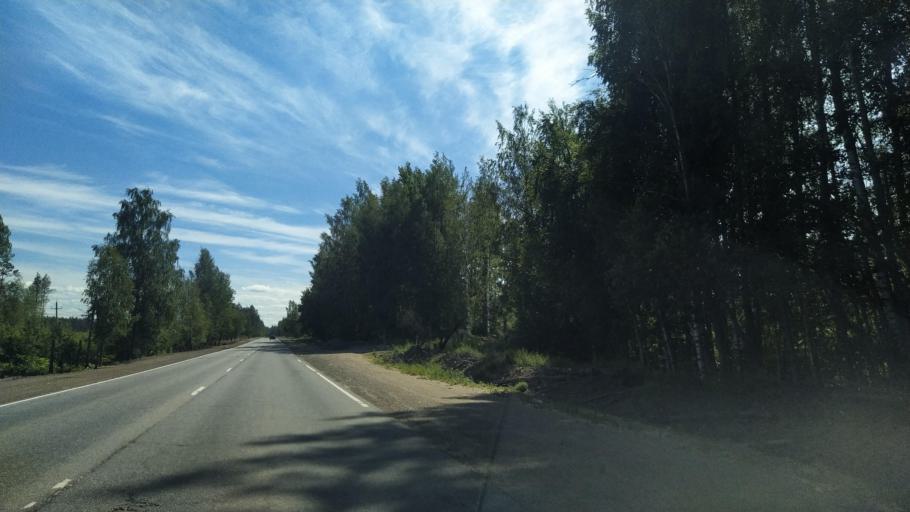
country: RU
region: Leningrad
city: Koltushi
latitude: 59.8796
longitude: 30.6776
